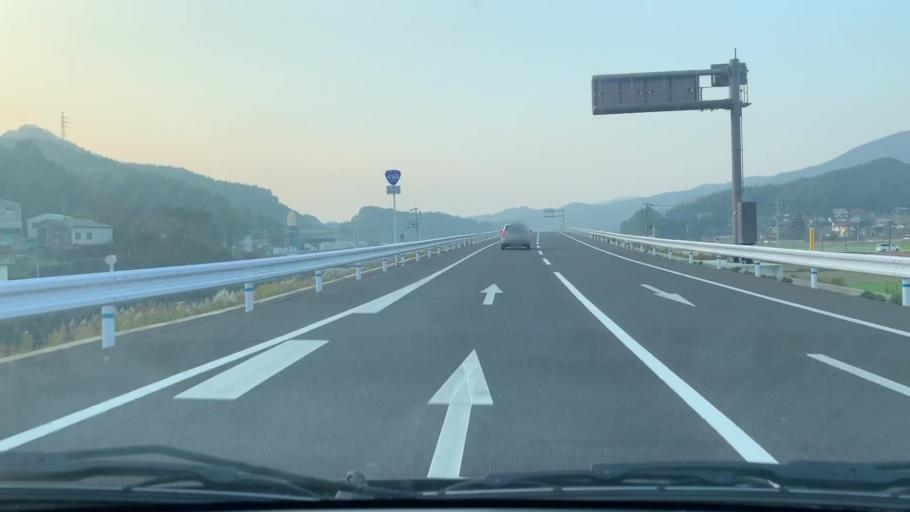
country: JP
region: Saga Prefecture
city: Takeocho-takeo
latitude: 33.2513
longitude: 129.9913
